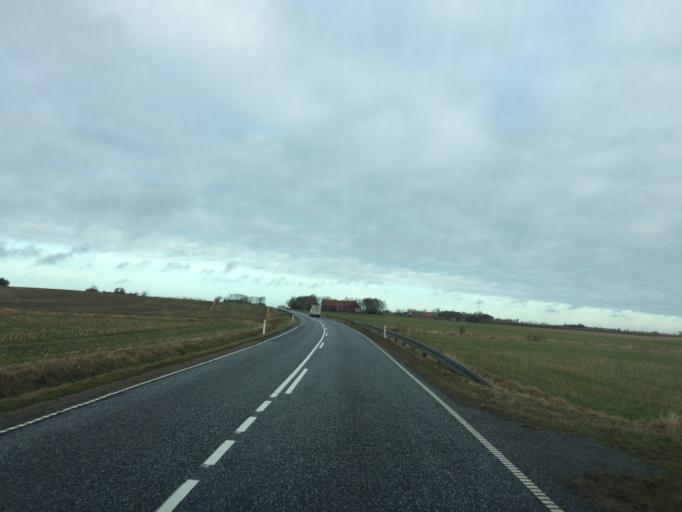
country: DK
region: Central Jutland
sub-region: Struer Kommune
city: Struer
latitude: 56.4421
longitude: 8.5315
